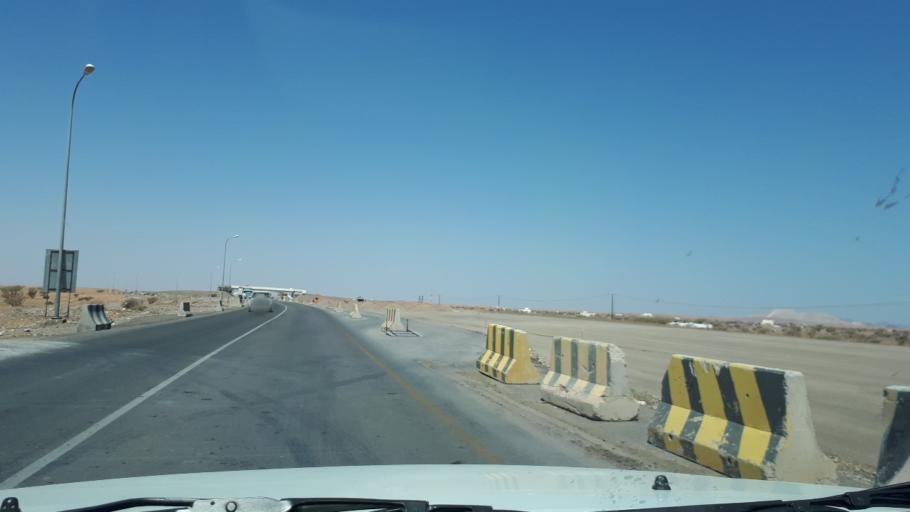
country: OM
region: Ash Sharqiyah
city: Badiyah
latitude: 22.4959
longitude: 58.9534
